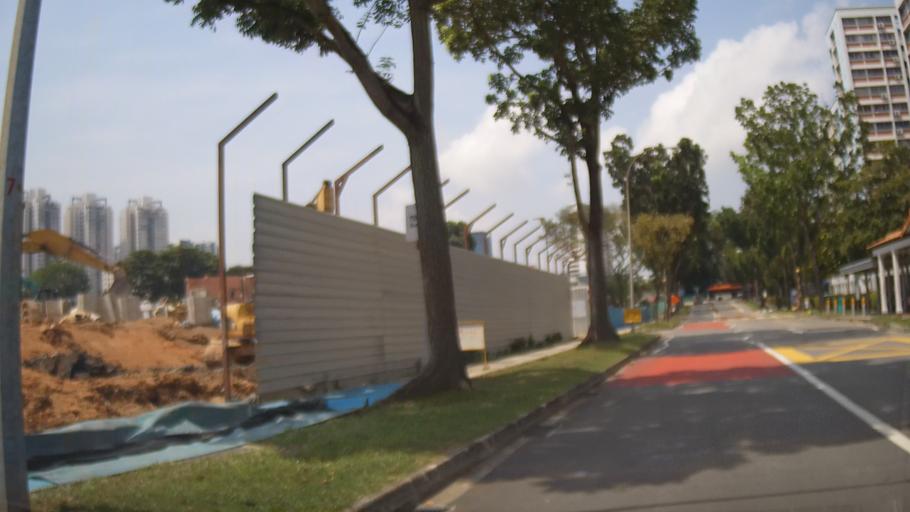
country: SG
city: Singapore
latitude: 1.3190
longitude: 103.8577
